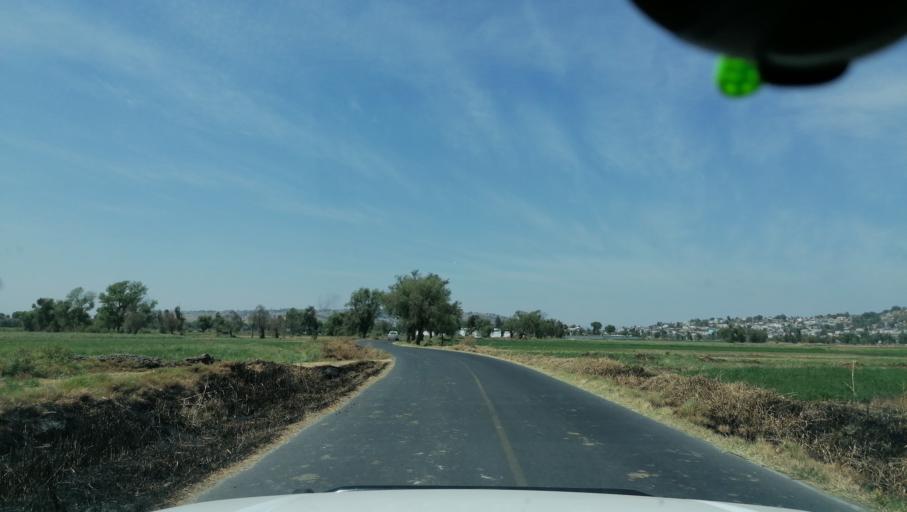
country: MX
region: Tlaxcala
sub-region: Tetlatlahuca
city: Tetlatlahuca
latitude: 19.2204
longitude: -98.2912
